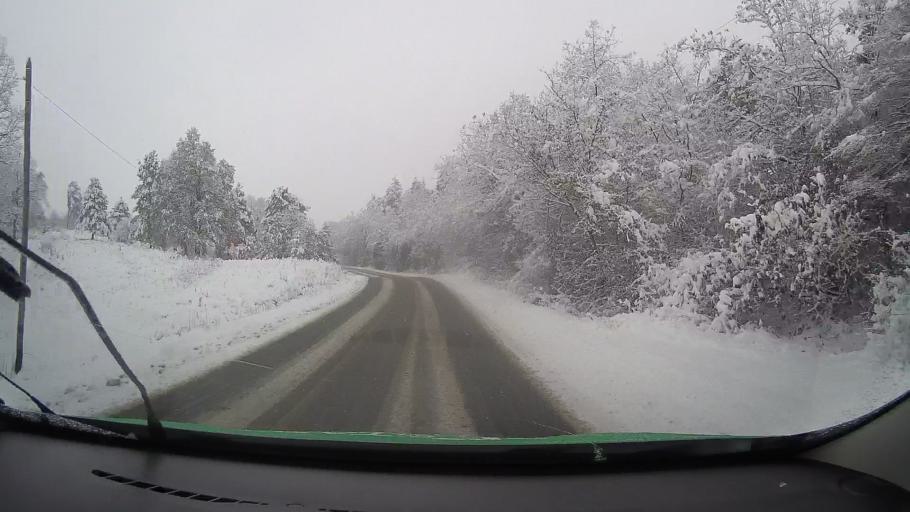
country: RO
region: Hunedoara
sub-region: Comuna Teliucu Inferior
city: Teliucu Inferior
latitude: 45.7066
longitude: 22.8820
